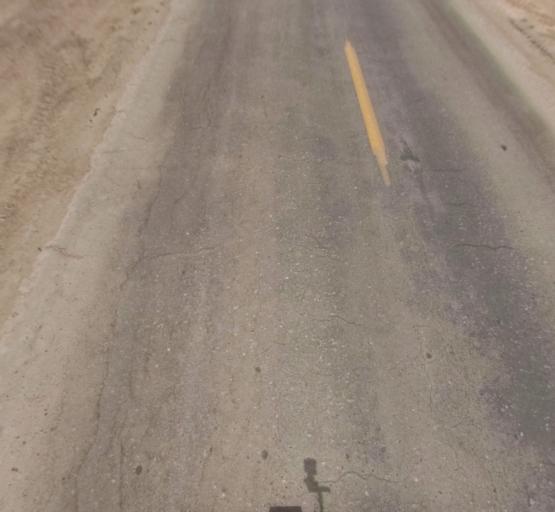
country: US
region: California
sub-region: Fresno County
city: Kerman
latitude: 36.8343
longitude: -120.1872
